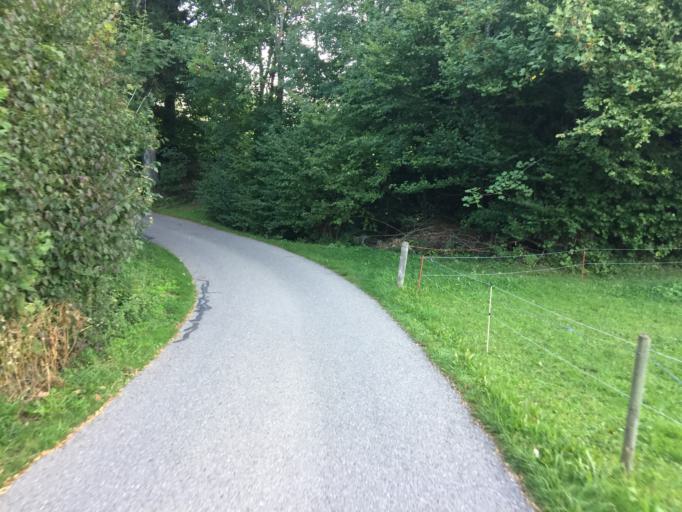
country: CH
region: Saint Gallen
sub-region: Wahlkreis Wil
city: Oberuzwil
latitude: 47.4131
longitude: 9.1454
